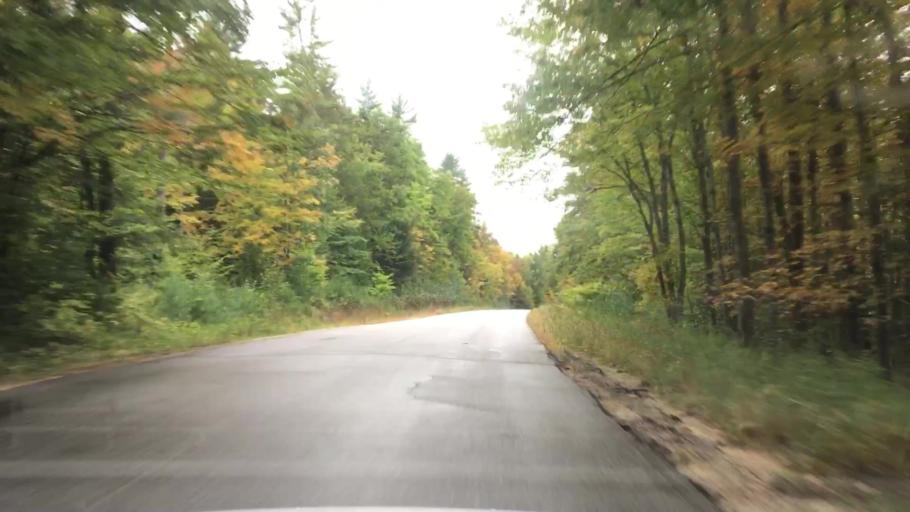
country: US
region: Maine
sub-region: Cumberland County
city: Harrison
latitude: 44.0200
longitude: -70.5878
